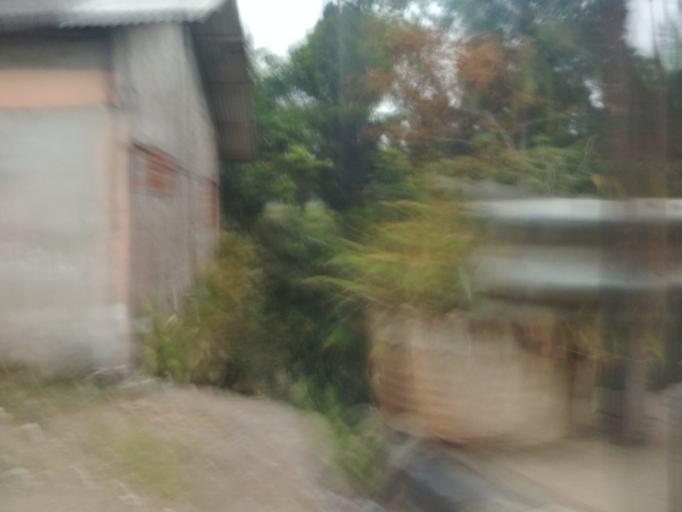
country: ID
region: West Java
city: Caringin
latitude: -6.7030
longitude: 106.8262
